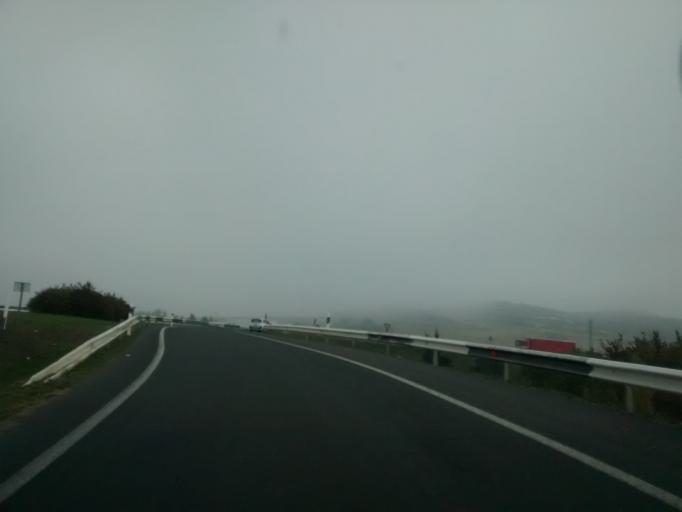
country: ES
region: Basque Country
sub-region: Provincia de Alava
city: Gasteiz / Vitoria
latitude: 42.8797
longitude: -2.6930
